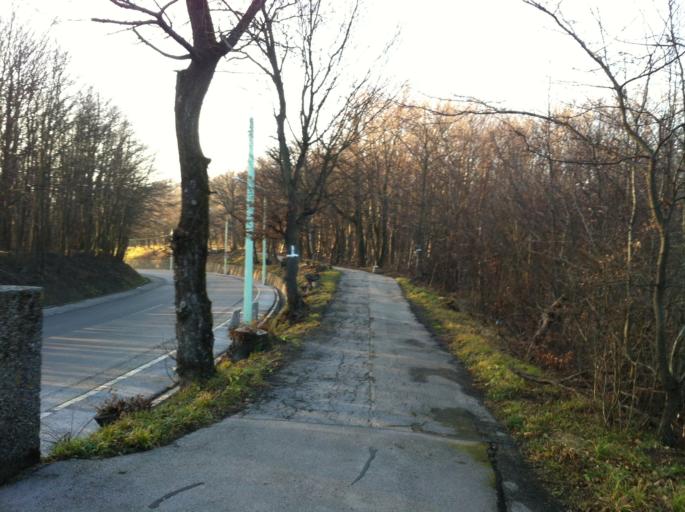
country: AT
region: Lower Austria
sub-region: Politischer Bezirk Wien-Umgebung
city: Klosterneuburg
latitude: 48.2773
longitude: 16.3258
